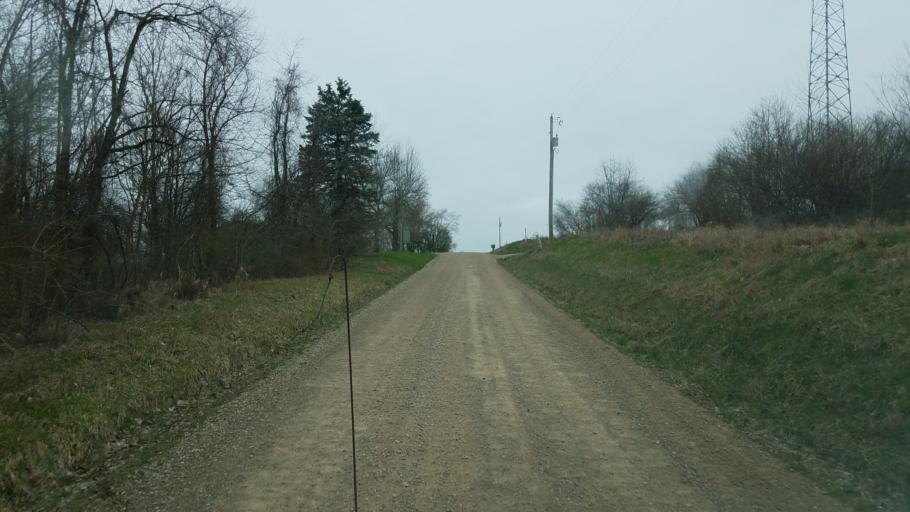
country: US
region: Ohio
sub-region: Knox County
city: Mount Vernon
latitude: 40.4650
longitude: -82.4361
